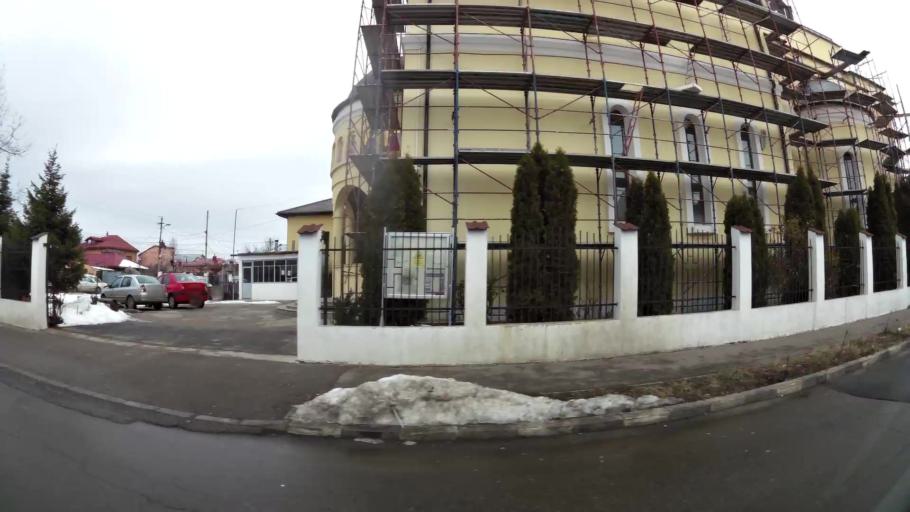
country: RO
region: Ilfov
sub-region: Comuna Pantelimon
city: Pantelimon
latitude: 44.4337
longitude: 26.1990
